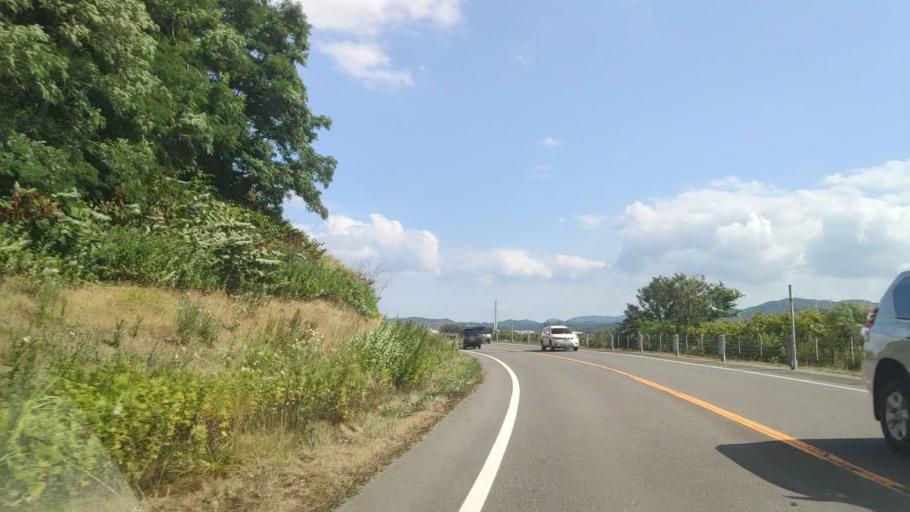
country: JP
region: Hokkaido
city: Rumoi
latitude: 43.9512
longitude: 141.6460
